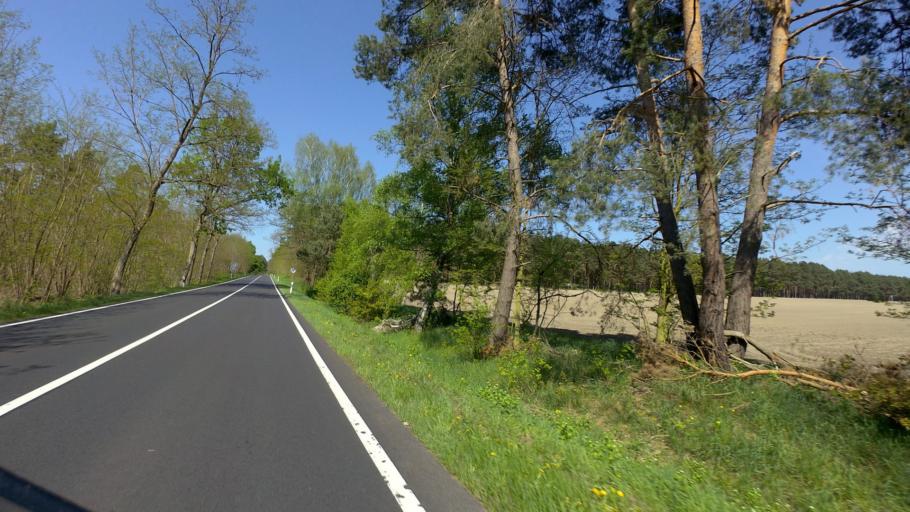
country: DE
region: Brandenburg
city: Lieberose
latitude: 52.0042
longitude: 14.3102
